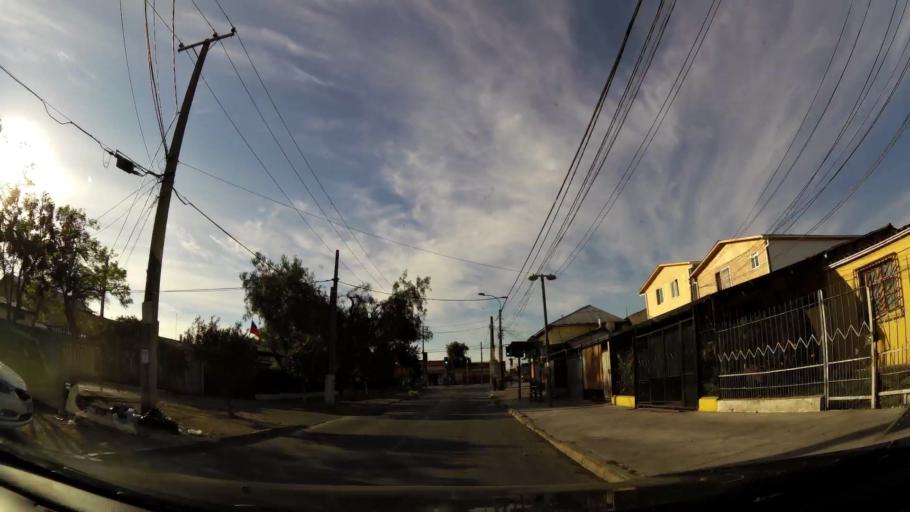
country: CL
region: Santiago Metropolitan
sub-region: Provincia de Cordillera
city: Puente Alto
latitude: -33.6148
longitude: -70.5783
